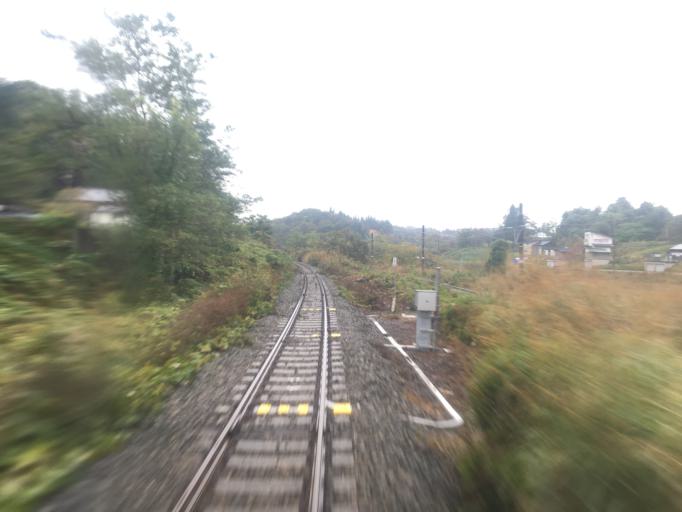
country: JP
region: Yamagata
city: Shinjo
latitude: 38.7156
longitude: 140.3144
